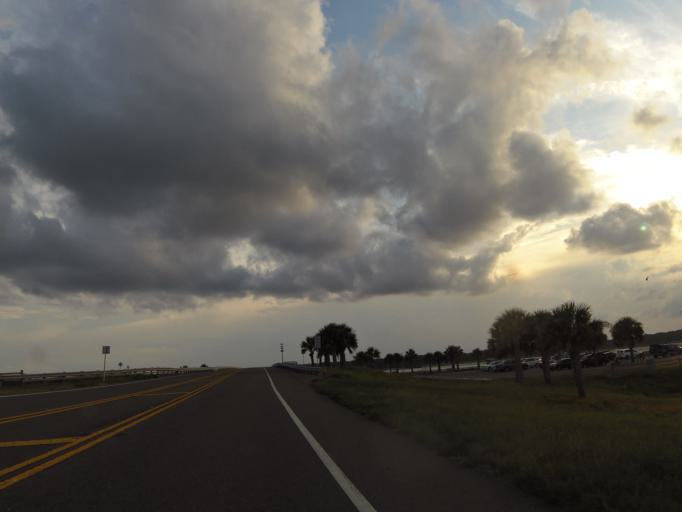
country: US
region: Florida
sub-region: Duval County
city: Atlantic Beach
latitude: 30.4228
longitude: -81.4139
